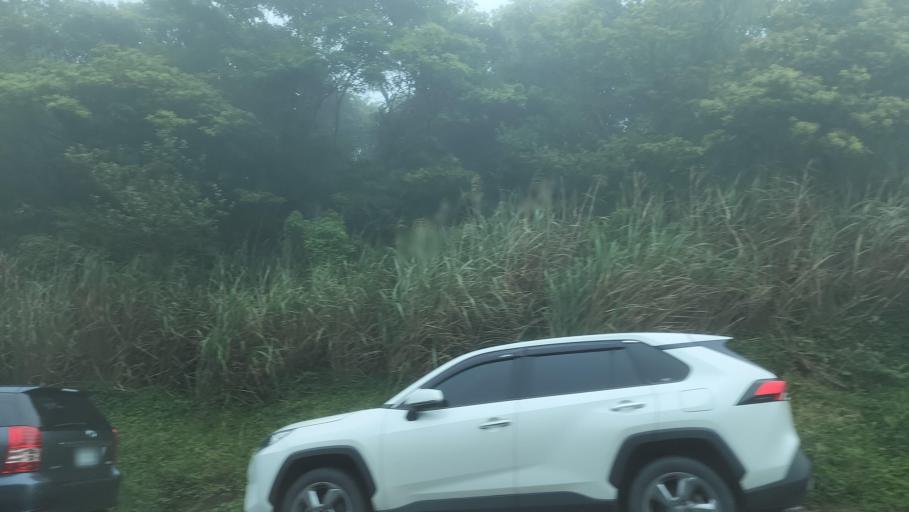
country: TW
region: Taipei
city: Taipei
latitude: 25.1378
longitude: 121.6032
